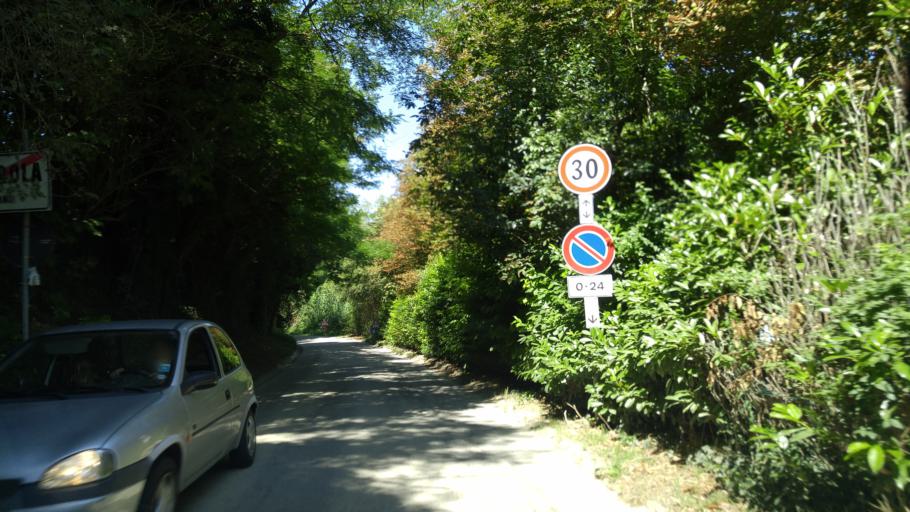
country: IT
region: The Marches
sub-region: Provincia di Pesaro e Urbino
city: Centinarola
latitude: 43.8330
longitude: 12.9786
